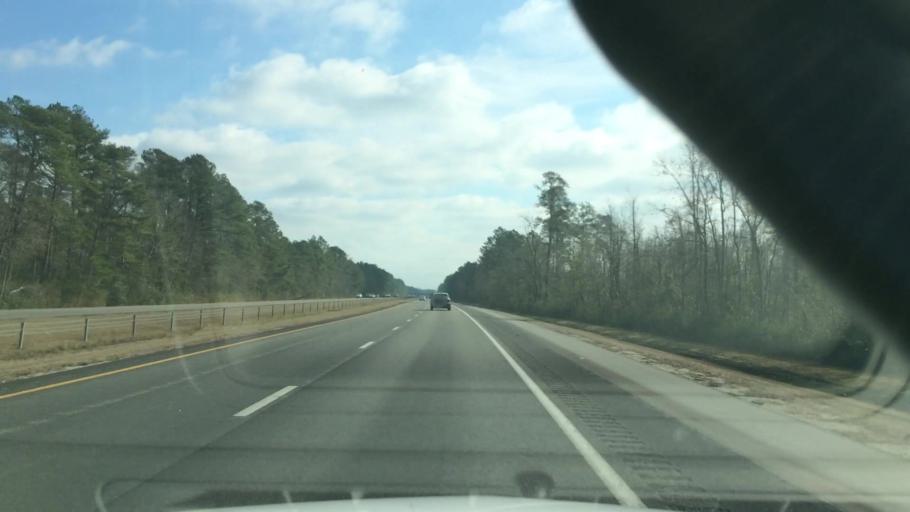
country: US
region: North Carolina
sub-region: Pender County
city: Burgaw
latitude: 34.6226
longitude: -77.9314
